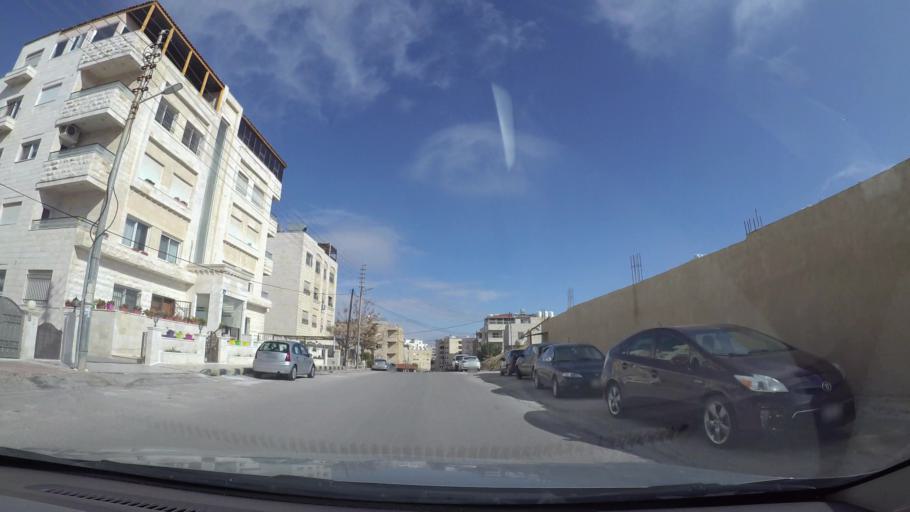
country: JO
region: Amman
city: Al Jubayhah
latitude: 32.0050
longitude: 35.8488
